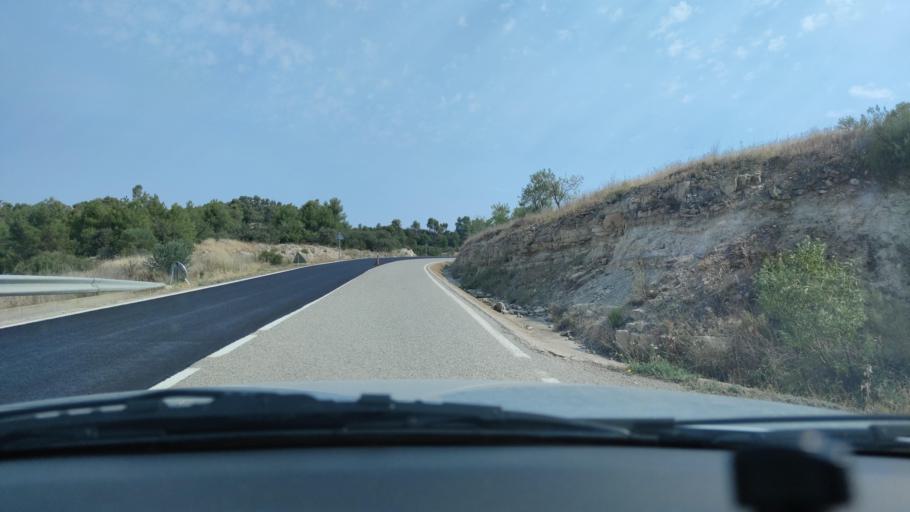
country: ES
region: Catalonia
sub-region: Provincia de Lleida
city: Fulleda
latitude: 41.5164
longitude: 1.0277
